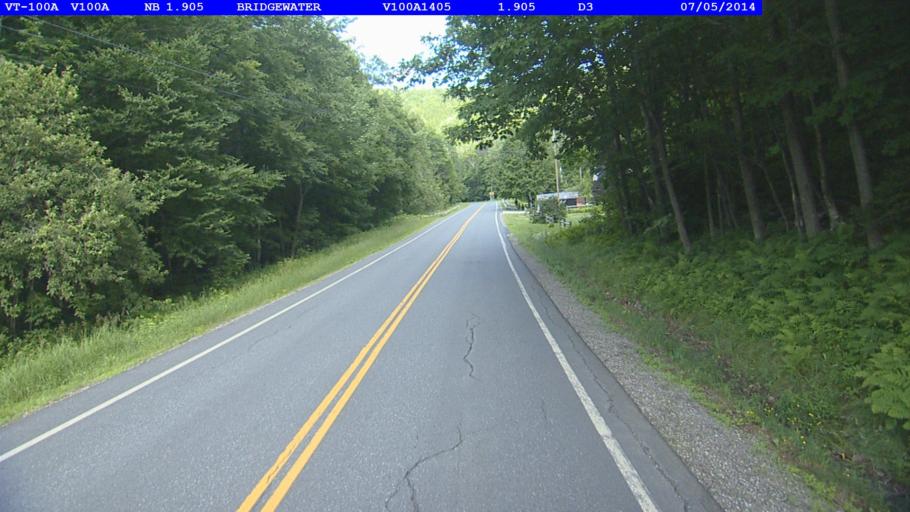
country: US
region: Vermont
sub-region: Windsor County
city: Woodstock
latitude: 43.5443
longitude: -72.7146
